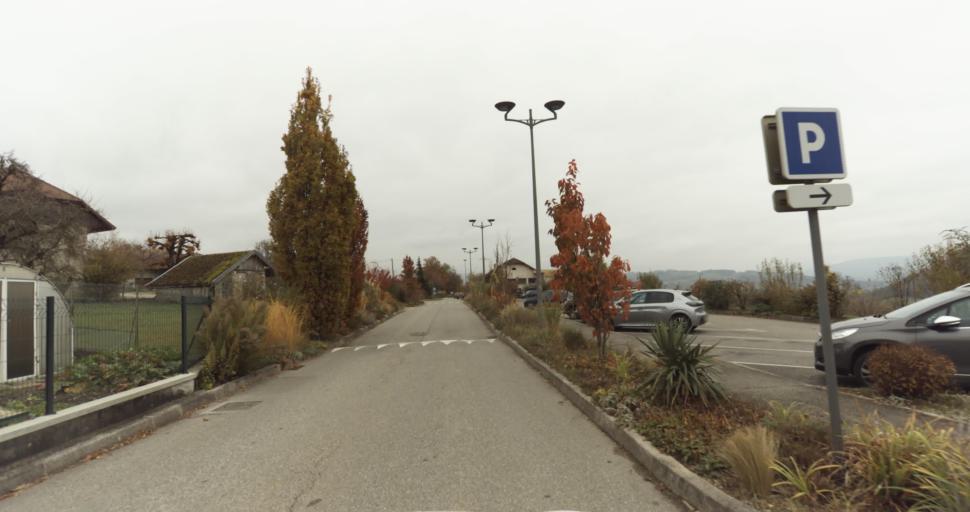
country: FR
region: Rhone-Alpes
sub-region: Departement de la Haute-Savoie
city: Alby-sur-Cheran
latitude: 45.8446
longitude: 6.0375
